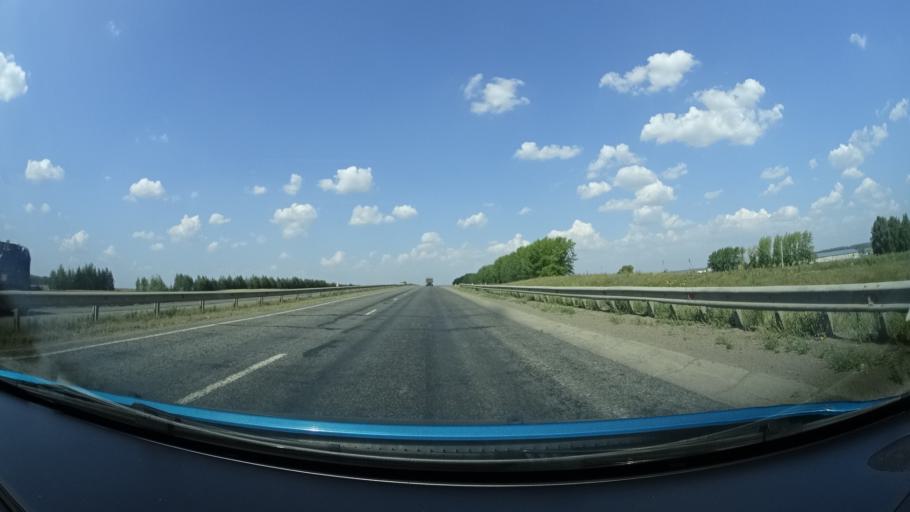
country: RU
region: Bashkortostan
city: Dmitriyevka
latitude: 54.6785
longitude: 55.3432
